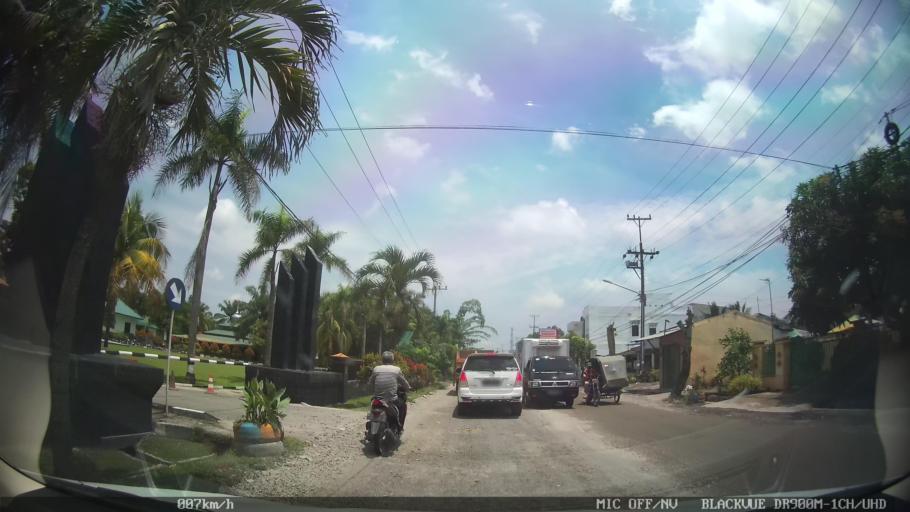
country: ID
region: North Sumatra
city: Perbaungan
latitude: 3.5393
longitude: 98.8824
